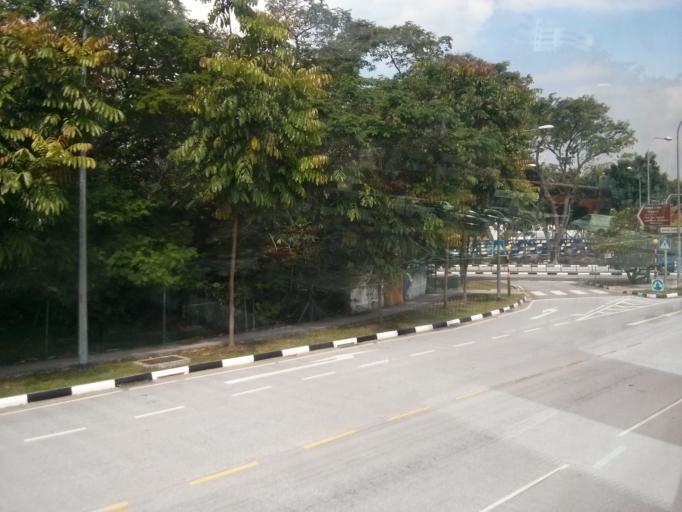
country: SG
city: Singapore
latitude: 1.3329
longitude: 103.7380
